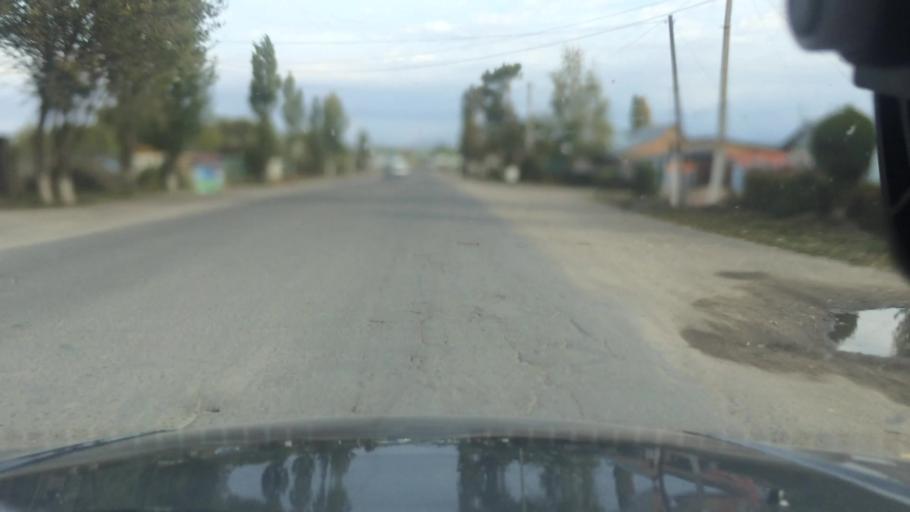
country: KG
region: Ysyk-Koel
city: Karakol
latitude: 42.5204
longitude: 78.3859
